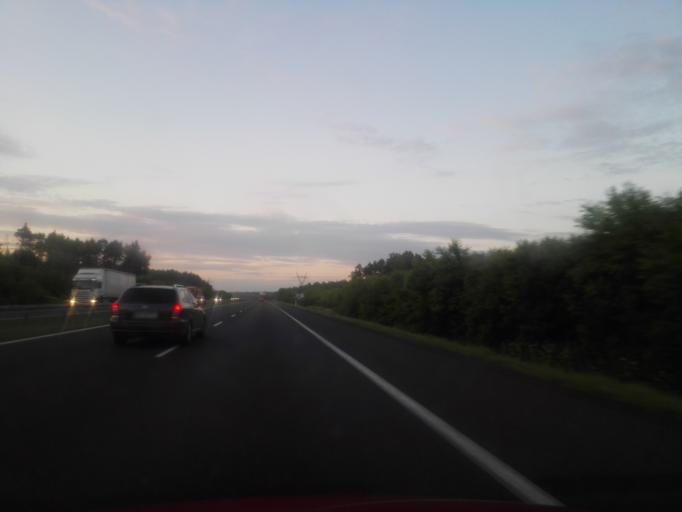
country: PL
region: Lodz Voivodeship
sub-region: Powiat radomszczanski
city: Radomsko
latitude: 51.0421
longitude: 19.3456
